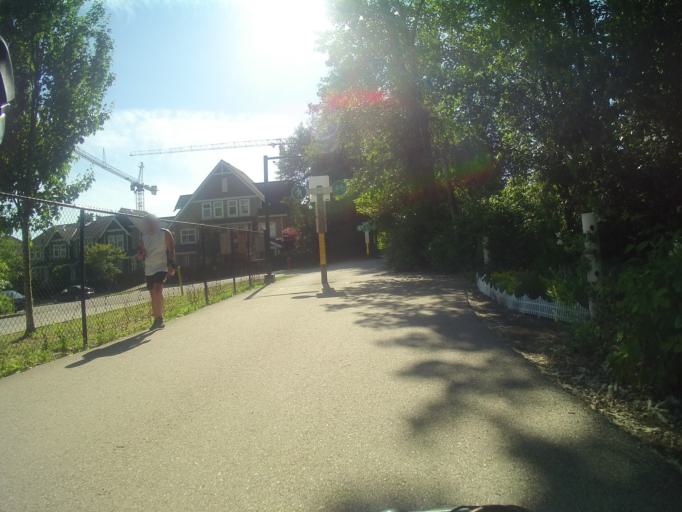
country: CA
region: British Columbia
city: Vancouver
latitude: 49.2177
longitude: -123.1107
